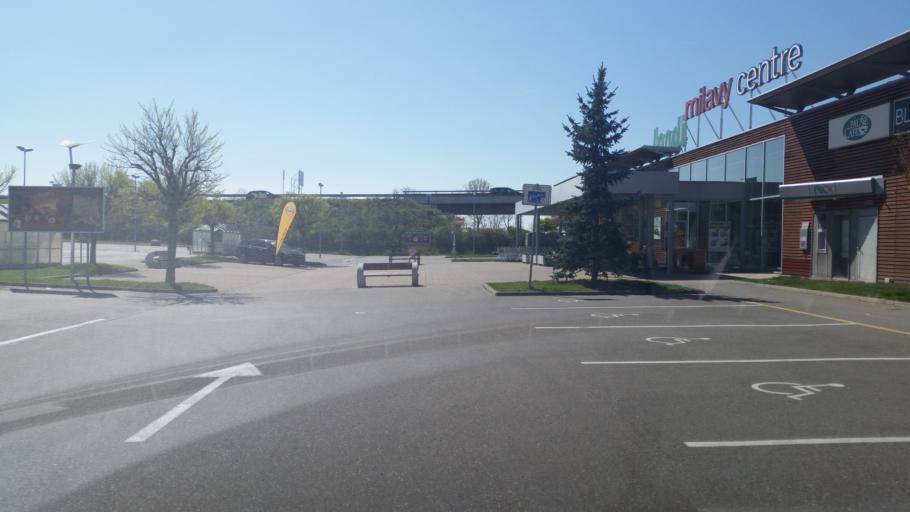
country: CH
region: Vaud
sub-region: Broye-Vully District
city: Avenches
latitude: 46.8807
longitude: 7.0422
